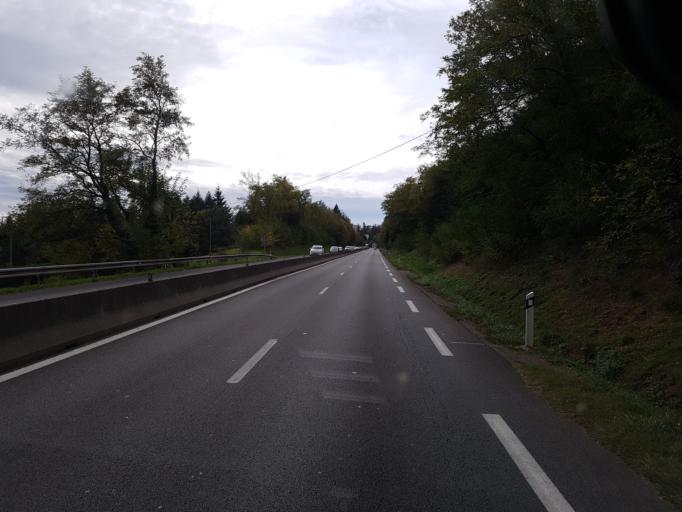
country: FR
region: Rhone-Alpes
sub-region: Departement de la Loire
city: Saint-Genest-Lerpt
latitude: 45.4556
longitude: 4.3382
